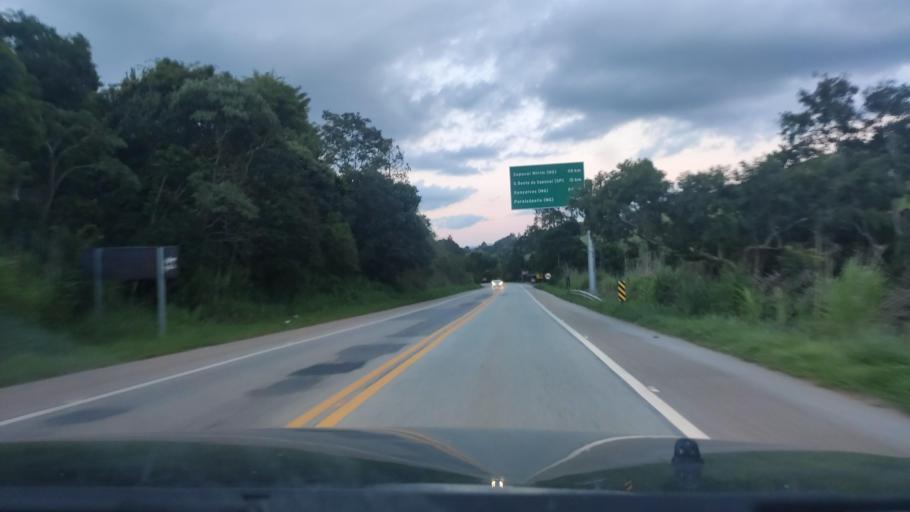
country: BR
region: Sao Paulo
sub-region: Campos Do Jordao
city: Campos do Jordao
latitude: -22.8090
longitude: -45.7529
